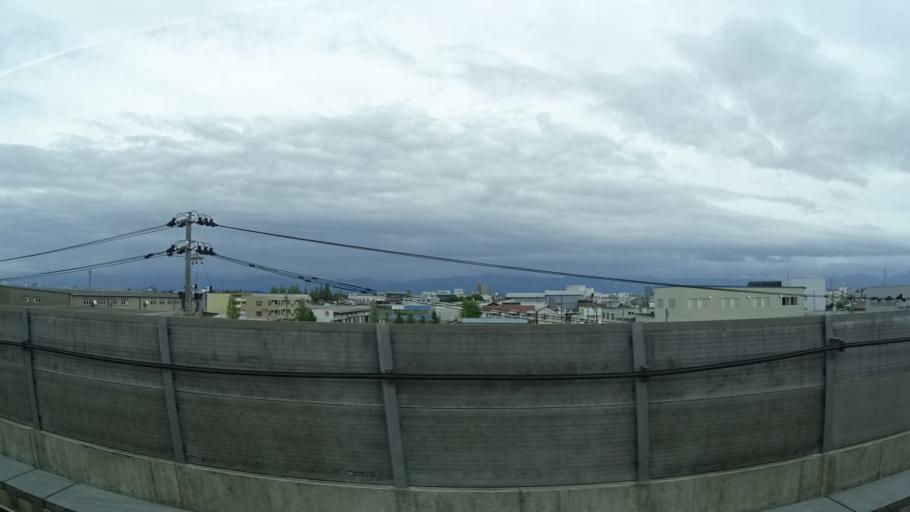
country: JP
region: Toyama
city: Toyama-shi
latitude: 36.7043
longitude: 137.2360
